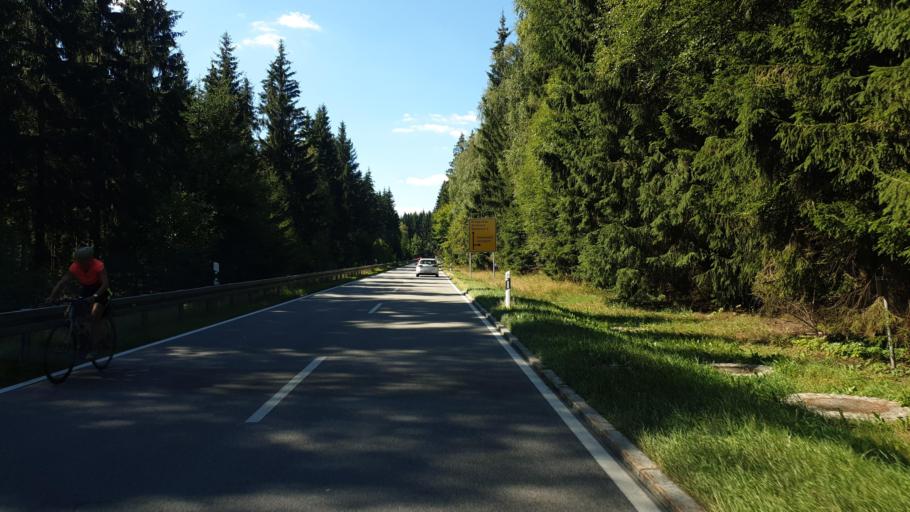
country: DE
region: Saxony
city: Hammerbrucke
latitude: 50.4266
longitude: 12.3997
